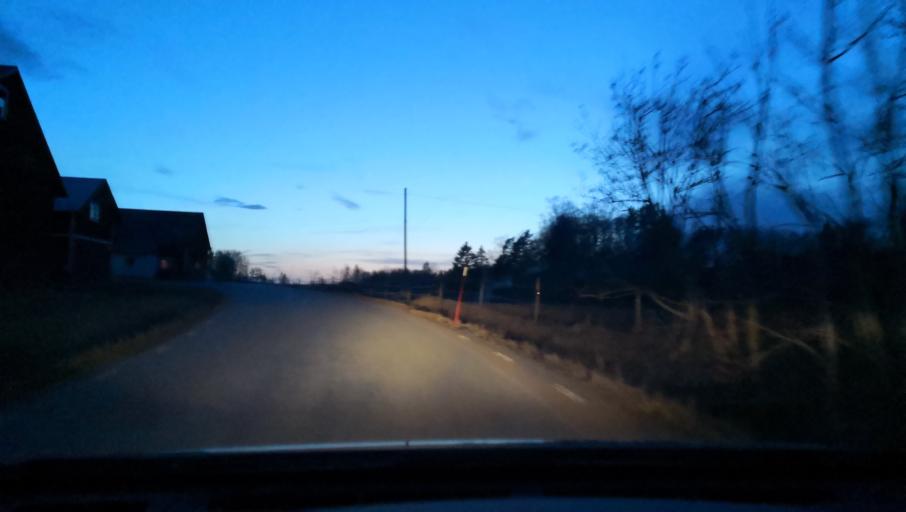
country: SE
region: Uppsala
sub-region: Enkopings Kommun
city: Grillby
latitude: 59.5983
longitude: 17.3072
